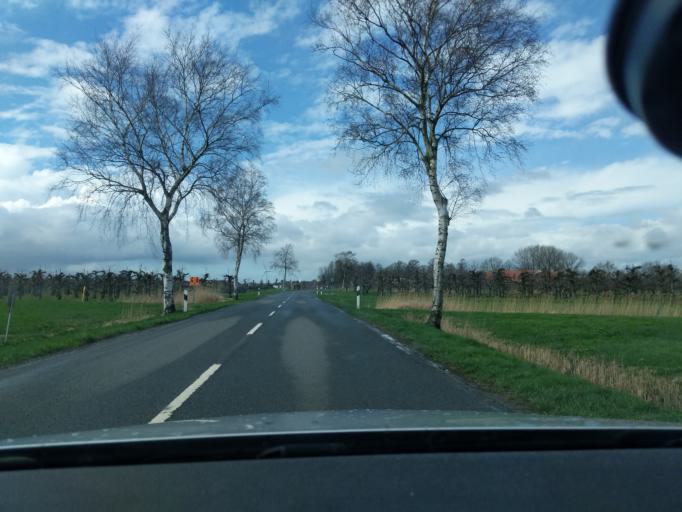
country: DE
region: Lower Saxony
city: Drochtersen
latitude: 53.7044
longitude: 9.3457
